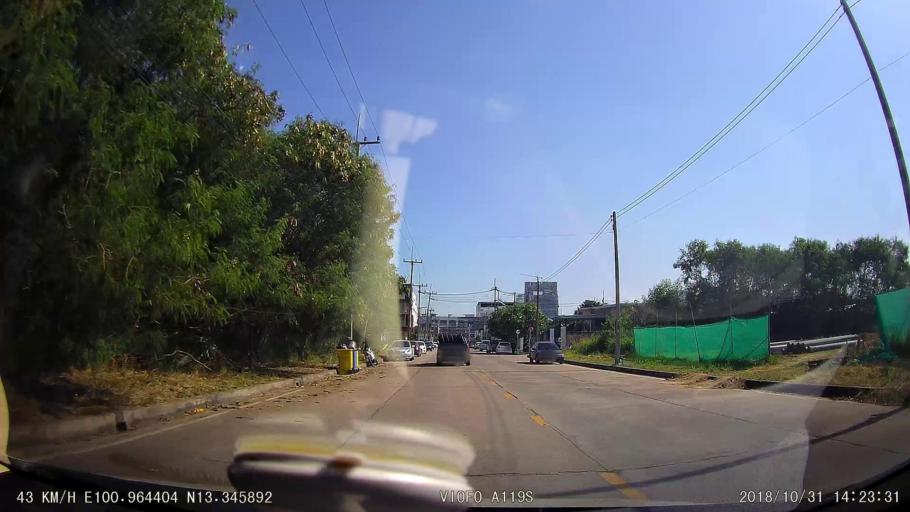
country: TH
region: Chon Buri
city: Chon Buri
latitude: 13.3458
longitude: 100.9645
